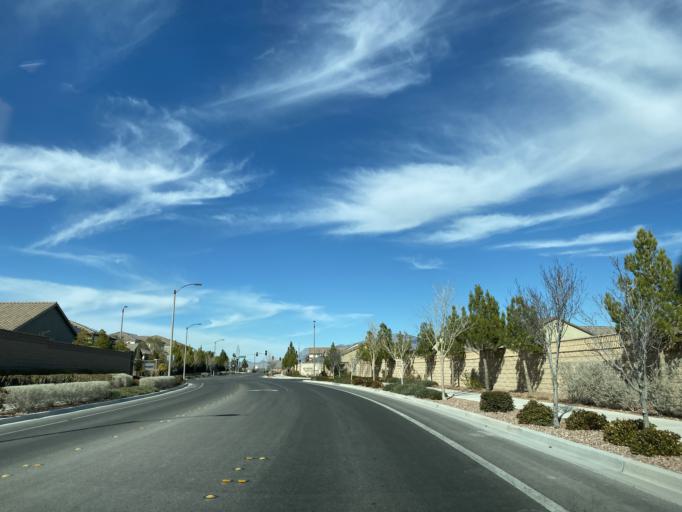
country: US
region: Nevada
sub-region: Clark County
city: Summerlin South
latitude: 36.3122
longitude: -115.3103
